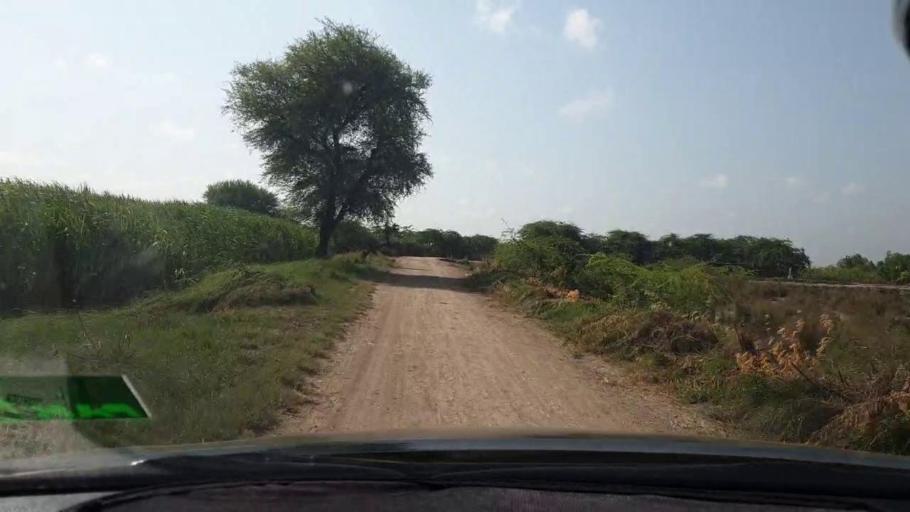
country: PK
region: Sindh
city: Tando Bago
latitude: 24.8767
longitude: 69.0107
